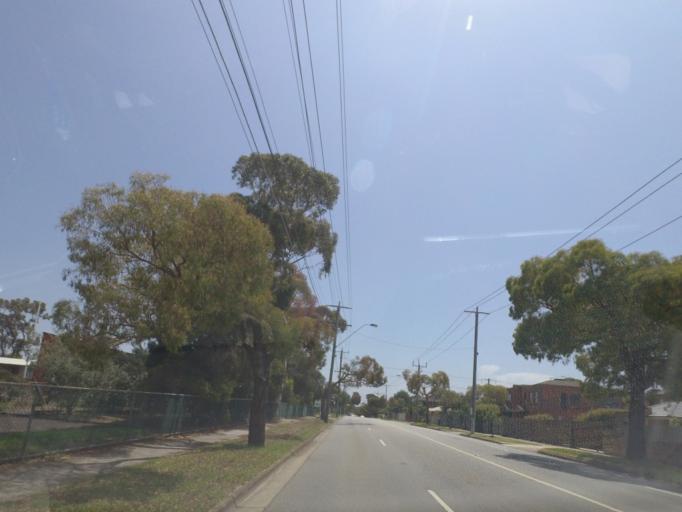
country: AU
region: Victoria
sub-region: Bayside
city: Hampton East
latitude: -37.9383
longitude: 145.0236
